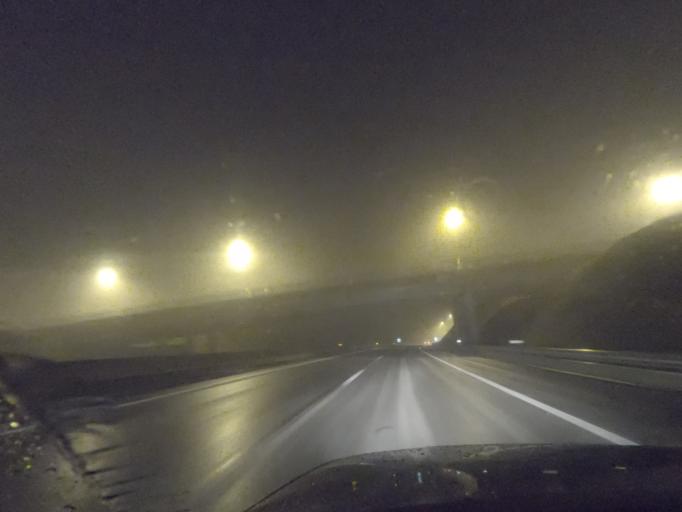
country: PT
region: Vila Real
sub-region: Vila Real
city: Vila Real
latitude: 41.2944
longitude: -7.6937
